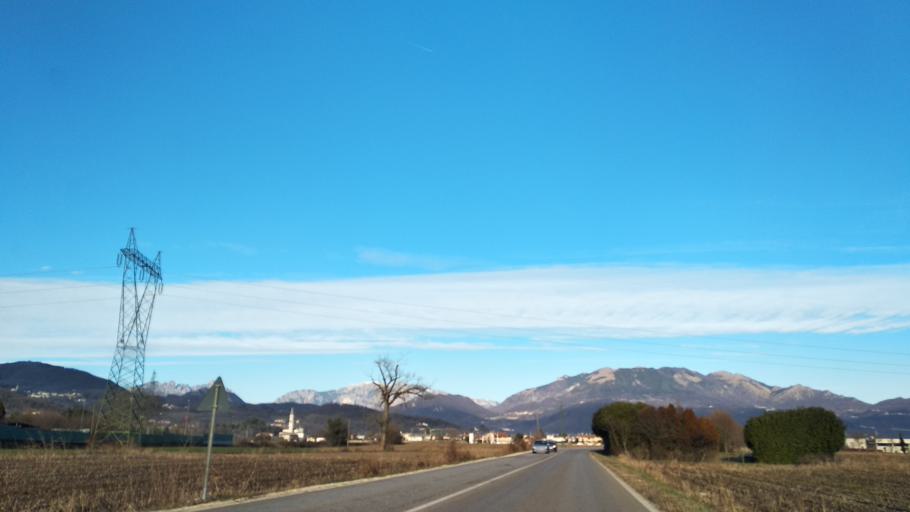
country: IT
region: Veneto
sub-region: Provincia di Vicenza
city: San Vito di Leguzzano
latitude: 45.6741
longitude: 11.3881
